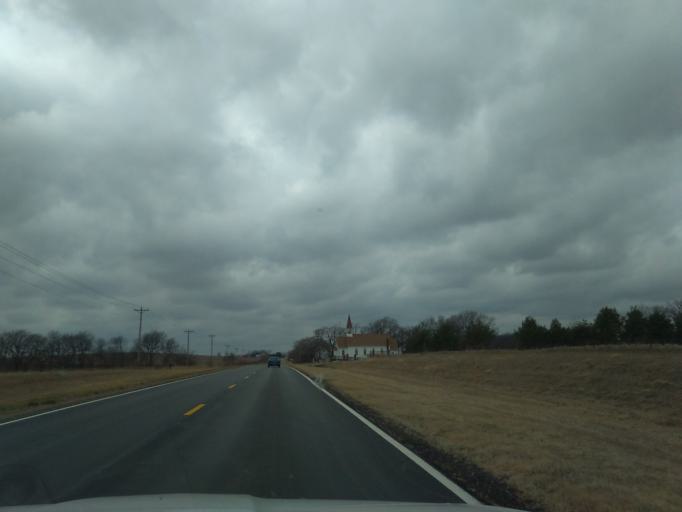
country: US
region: Kansas
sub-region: Nemaha County
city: Sabetha
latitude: 40.0588
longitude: -95.9434
